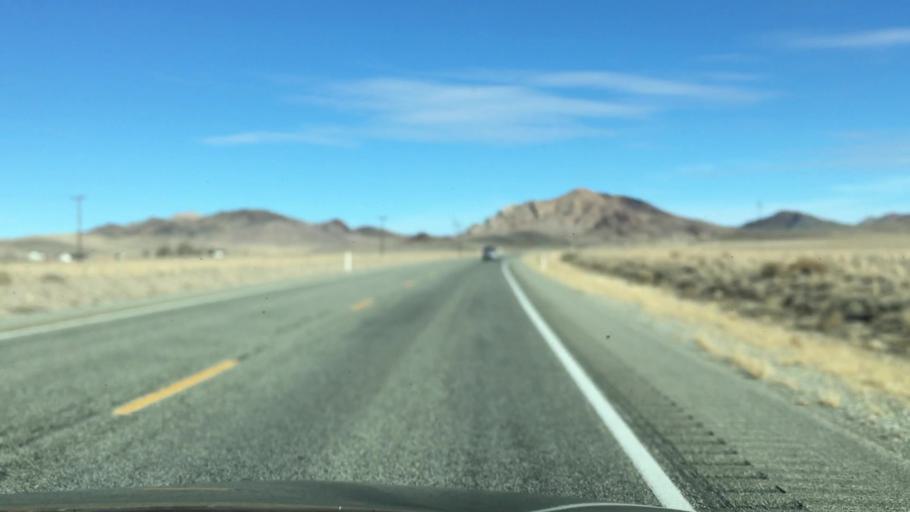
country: US
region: Nevada
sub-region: Lyon County
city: Yerington
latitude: 39.0294
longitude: -119.0397
